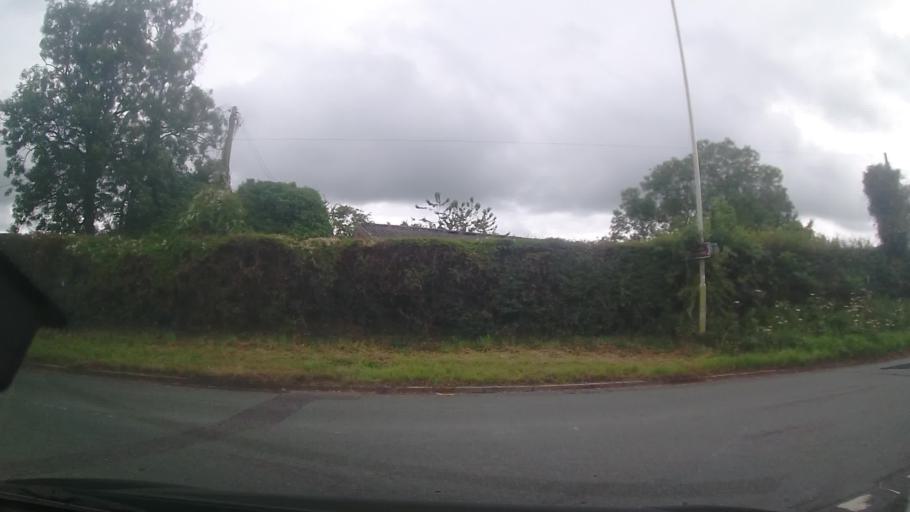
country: GB
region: England
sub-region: Shropshire
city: Whitchurch
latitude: 52.9678
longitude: -2.7021
